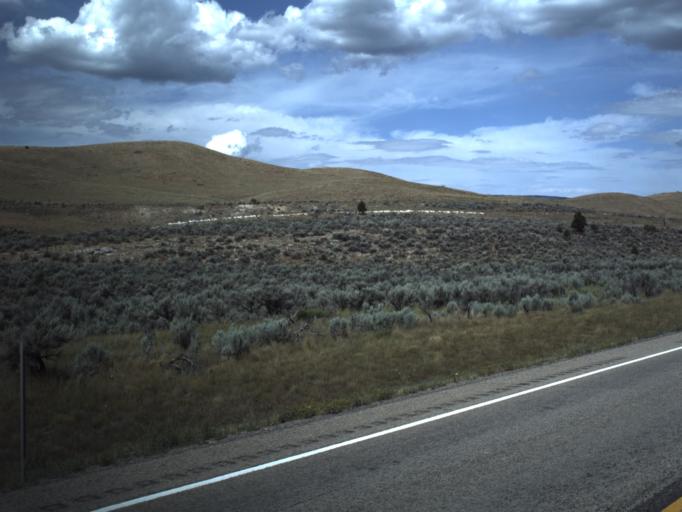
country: US
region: Utah
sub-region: Sanpete County
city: Fairview
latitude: 39.7302
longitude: -111.4755
